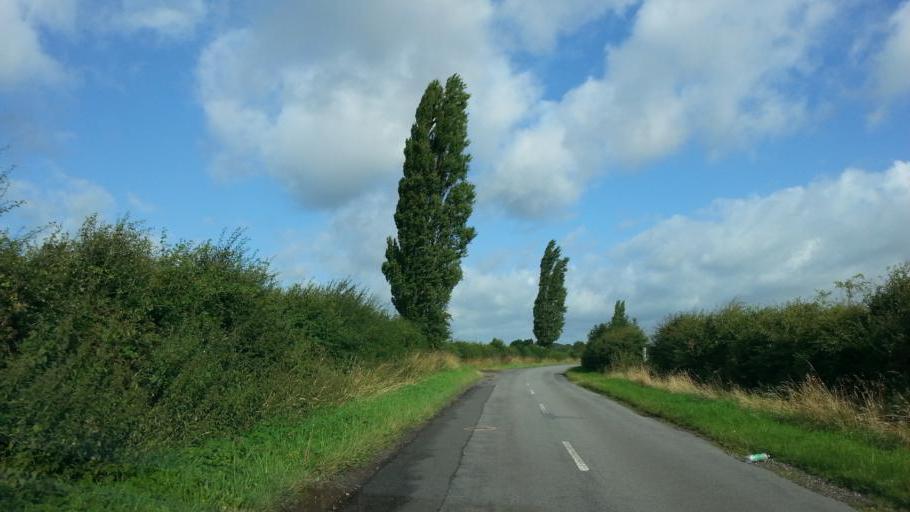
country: GB
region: England
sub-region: Nottinghamshire
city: Farndon
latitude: 53.0176
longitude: -0.8626
